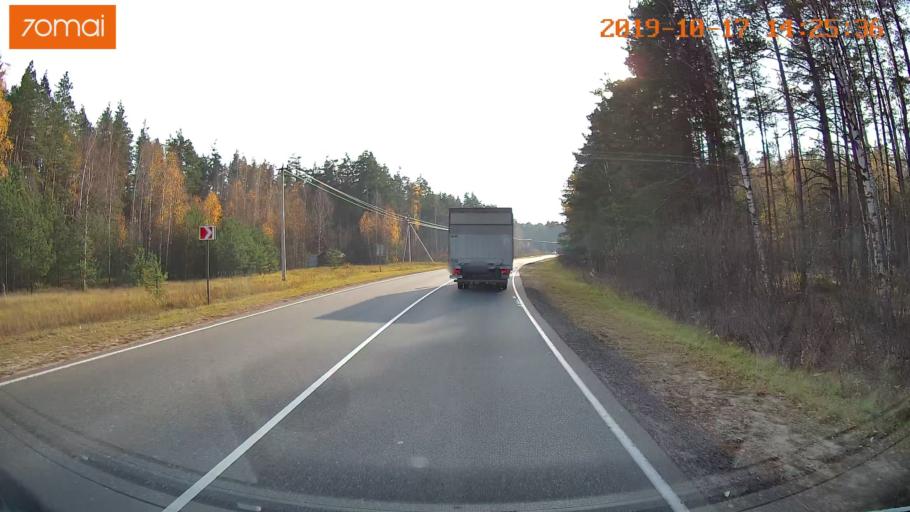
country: RU
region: Moskovskaya
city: Radovitskiy
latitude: 54.9989
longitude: 39.9765
